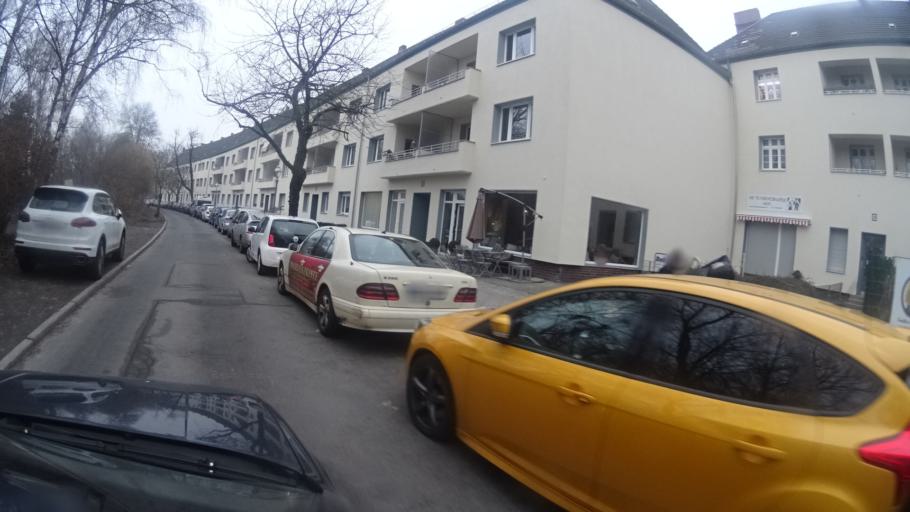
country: DE
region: Berlin
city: Schoneberg Bezirk
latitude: 52.4771
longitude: 13.3745
